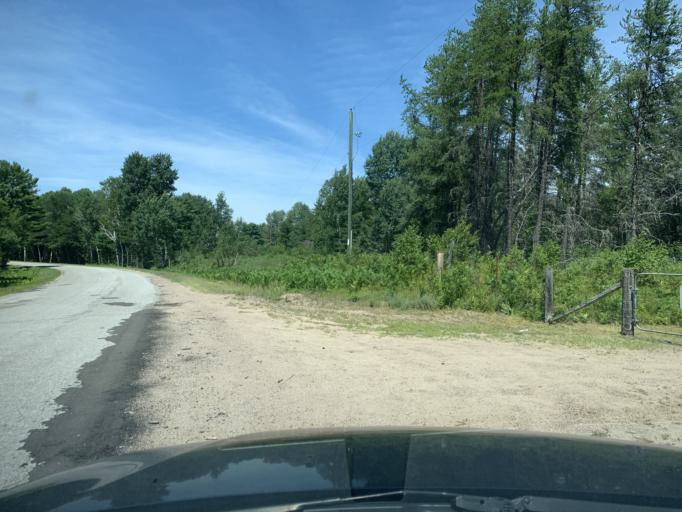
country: CA
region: Ontario
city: Petawawa
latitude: 45.6617
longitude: -77.6068
